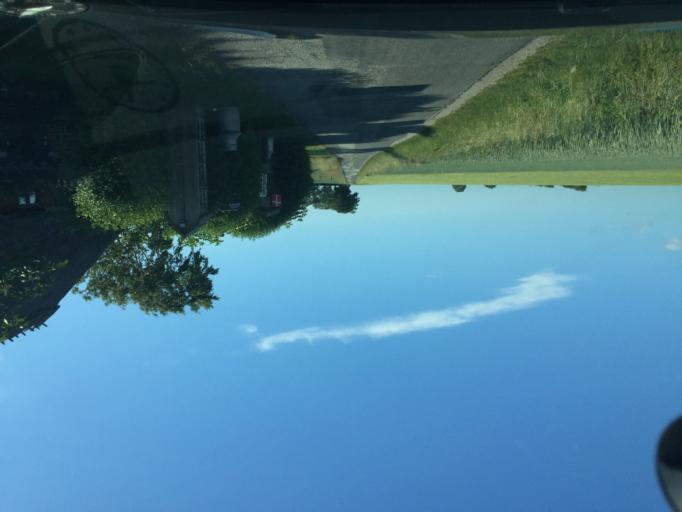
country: DK
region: Zealand
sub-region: Slagelse Kommune
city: Skaelskor
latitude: 55.2048
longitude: 11.1881
